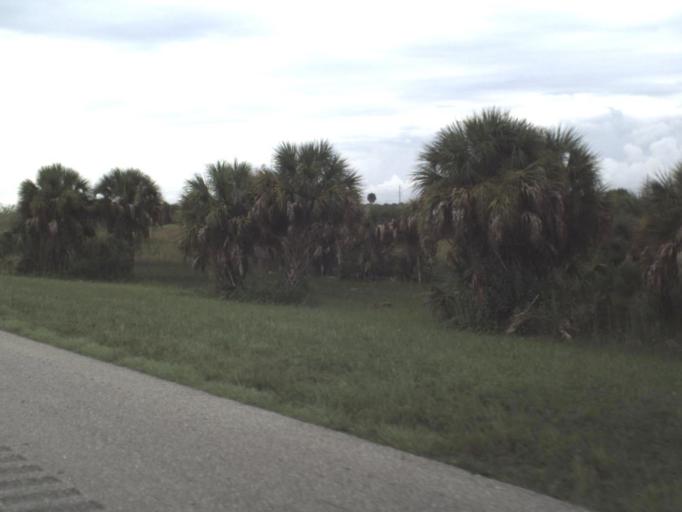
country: US
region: Florida
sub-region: Sarasota County
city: Osprey
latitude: 27.2076
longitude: -82.4434
